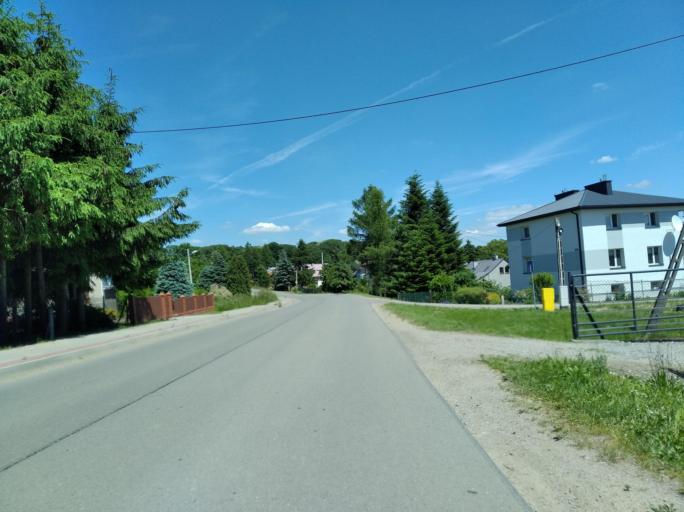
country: PL
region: Subcarpathian Voivodeship
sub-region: Powiat jasielski
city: Tarnowiec
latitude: 49.7575
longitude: 21.5916
